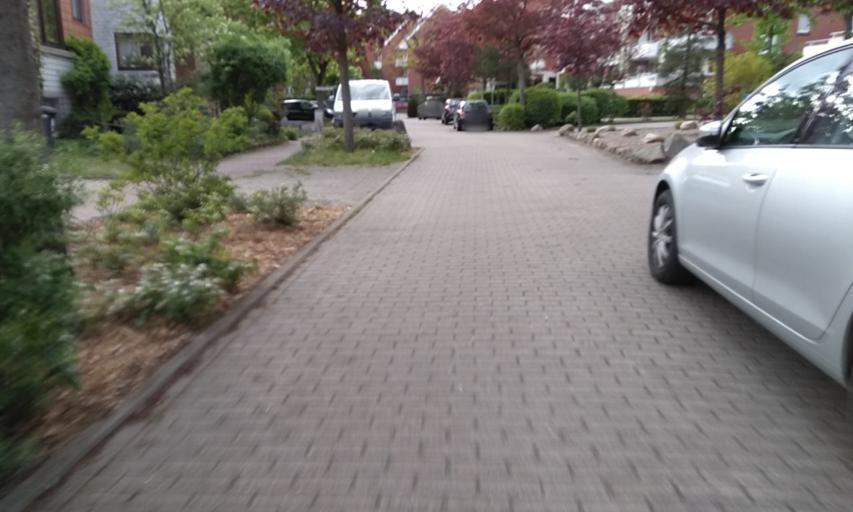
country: DE
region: Lower Saxony
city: Buxtehude
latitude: 53.4728
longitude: 9.7009
